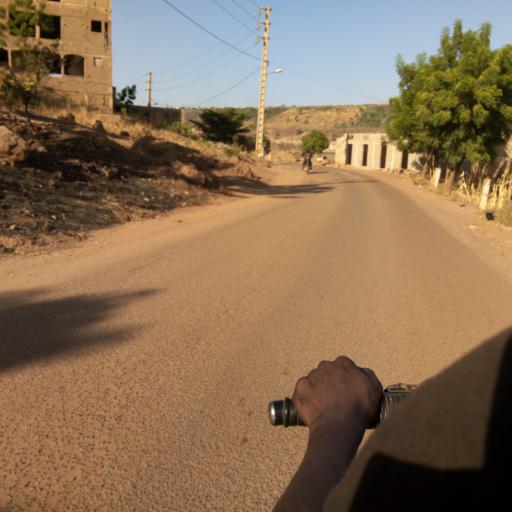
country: ML
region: Bamako
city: Bamako
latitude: 12.6585
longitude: -8.0385
